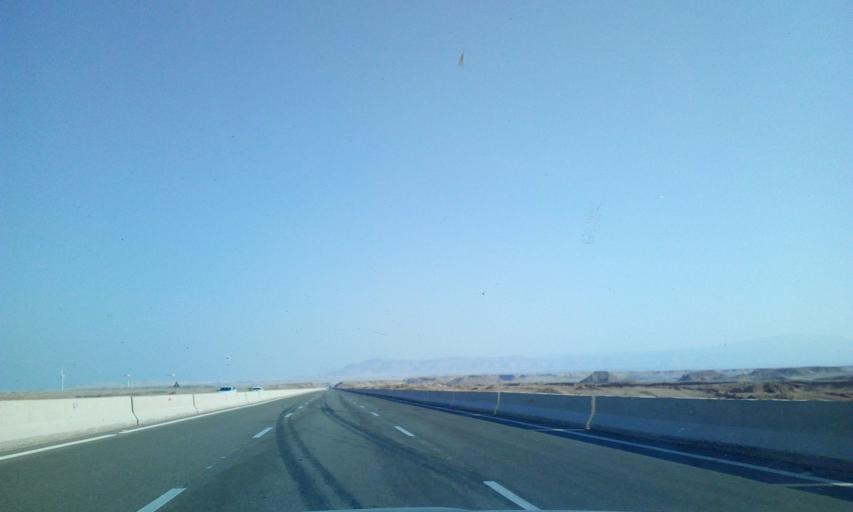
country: EG
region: As Suways
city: Ain Sukhna
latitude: 29.1764
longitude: 32.5046
